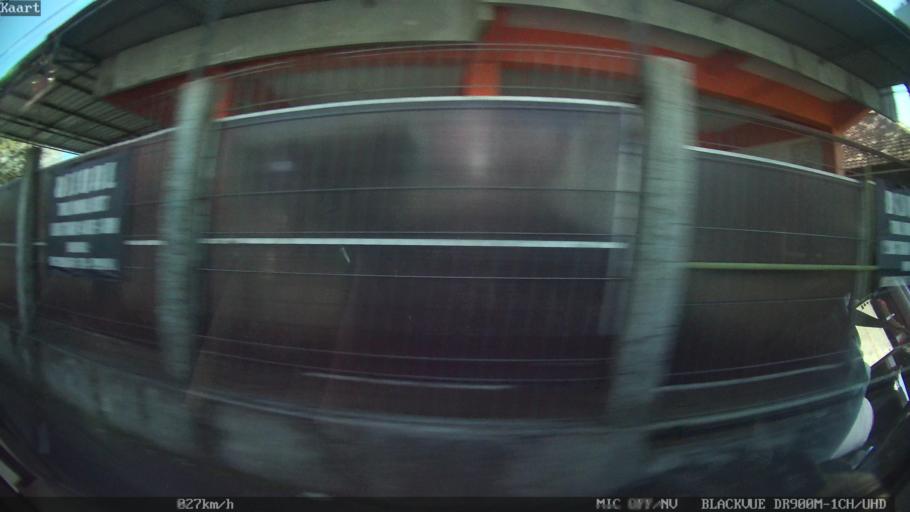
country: ID
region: Bali
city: Denpasar
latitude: -8.6488
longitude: 115.1902
